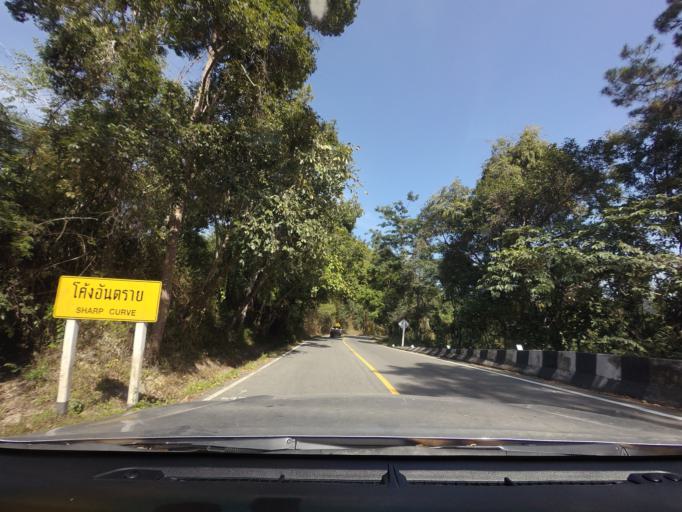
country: TH
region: Mae Hong Son
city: Mae Hi
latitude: 19.2312
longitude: 98.6666
